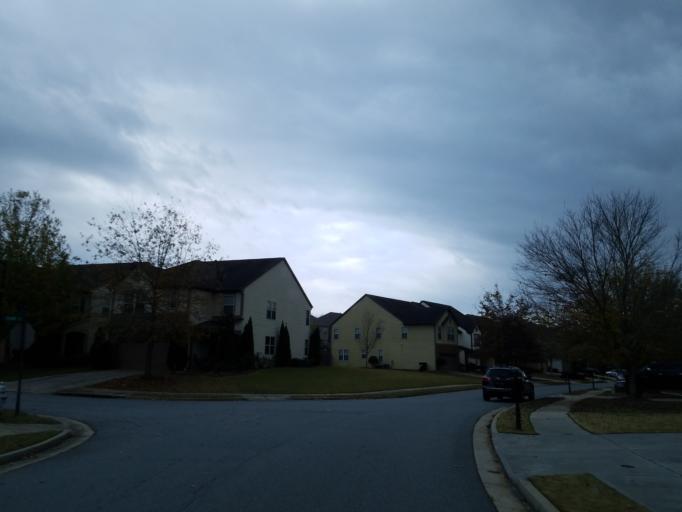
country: US
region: Georgia
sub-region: Cobb County
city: Acworth
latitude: 34.0933
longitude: -84.6247
